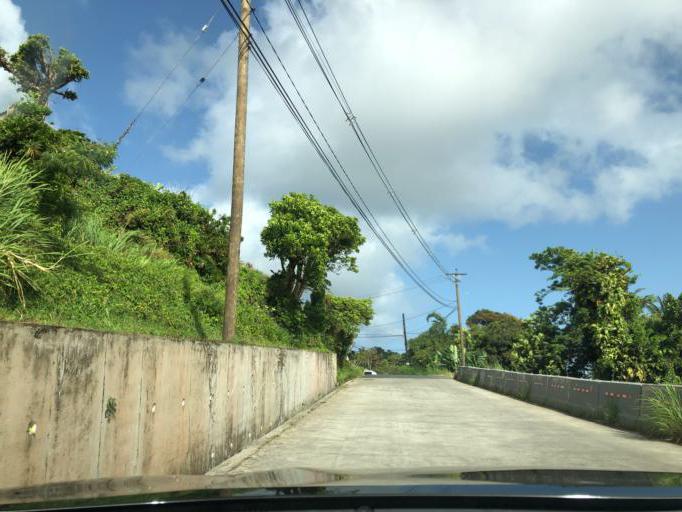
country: LC
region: Castries Quarter
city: Bisee
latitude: 13.9905
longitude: -60.9627
